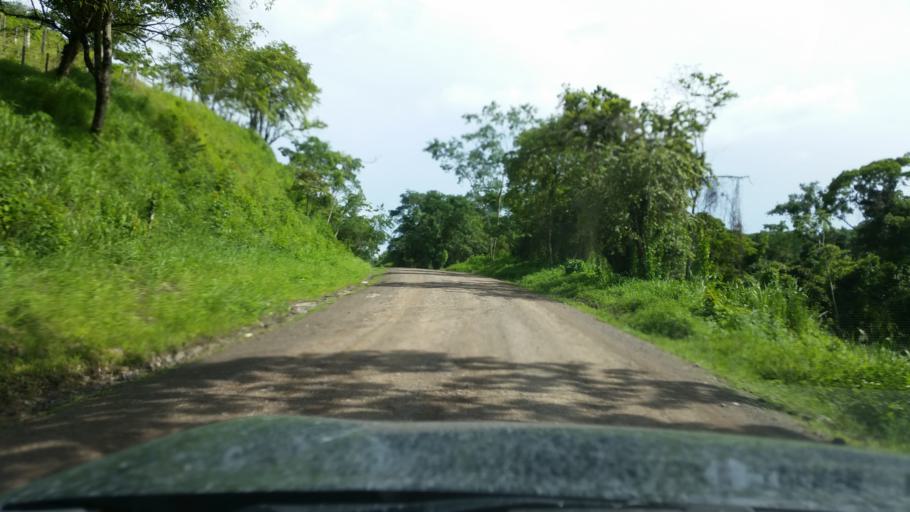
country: NI
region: Atlantico Norte (RAAN)
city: Siuna
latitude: 13.6689
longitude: -84.7922
